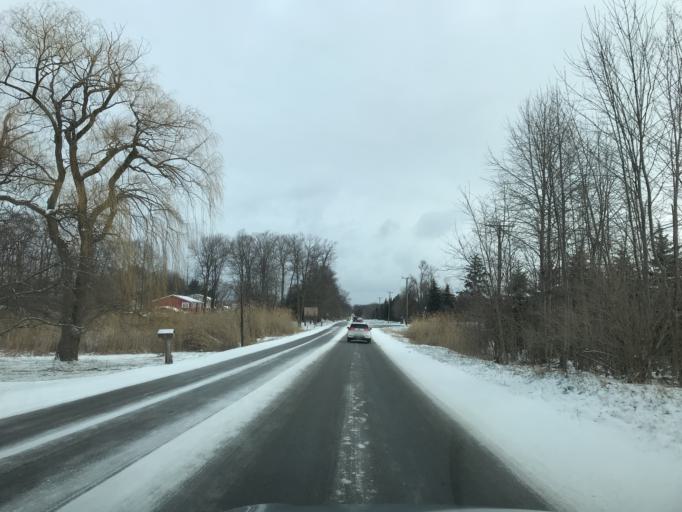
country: US
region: Michigan
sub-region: Oakland County
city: Wixom
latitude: 42.4739
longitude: -83.5541
